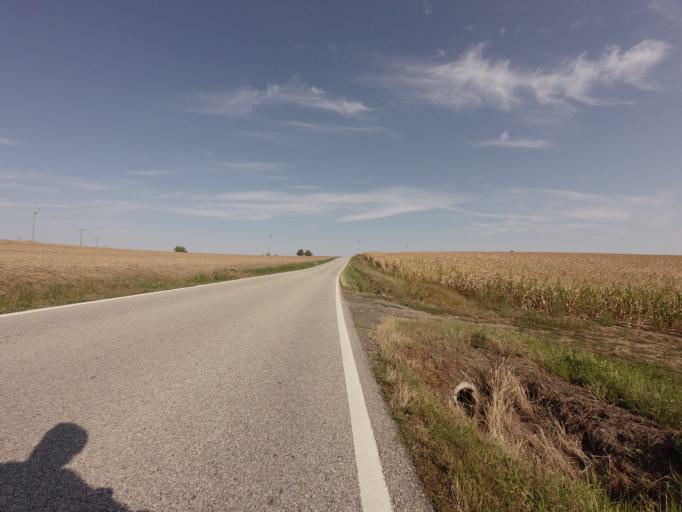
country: CZ
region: Jihocesky
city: Tyn nad Vltavou
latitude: 49.2888
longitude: 14.3929
